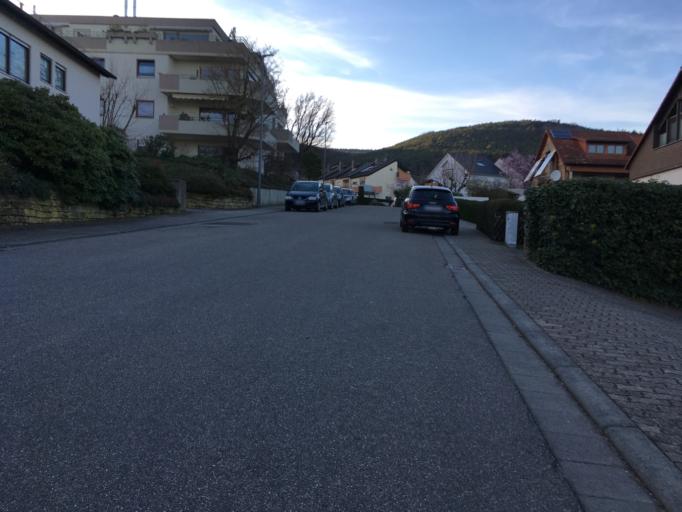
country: DE
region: Rheinland-Pfalz
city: Deidesheim
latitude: 49.3840
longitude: 8.1616
